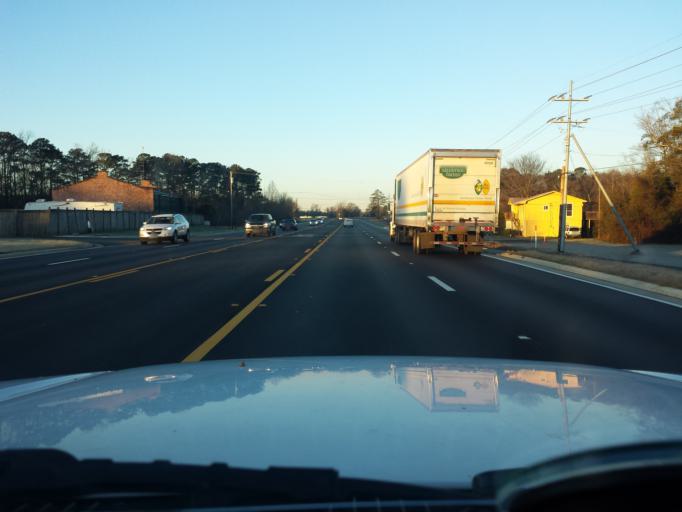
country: US
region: Mississippi
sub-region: Rankin County
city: Flowood
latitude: 32.3200
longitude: -90.1254
